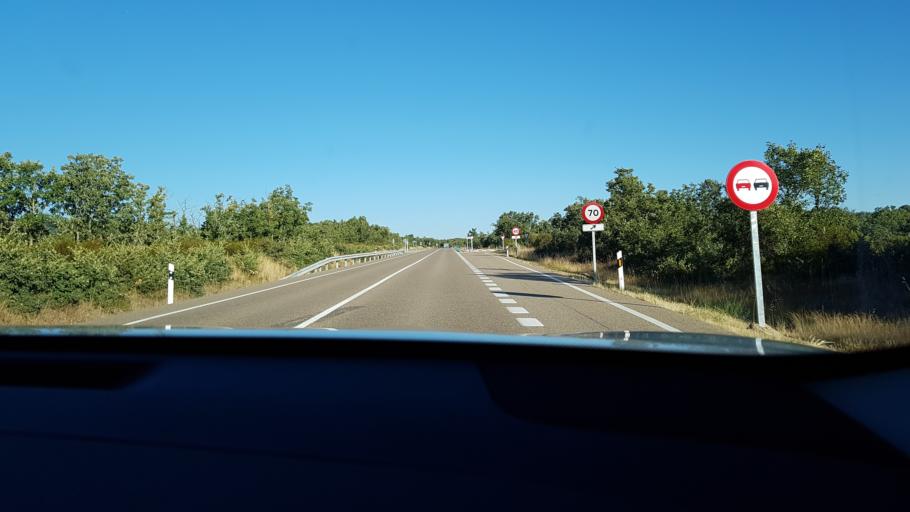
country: ES
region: Castille and Leon
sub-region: Provincia de Zamora
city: Samir de los Canos
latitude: 41.6684
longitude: -6.2246
